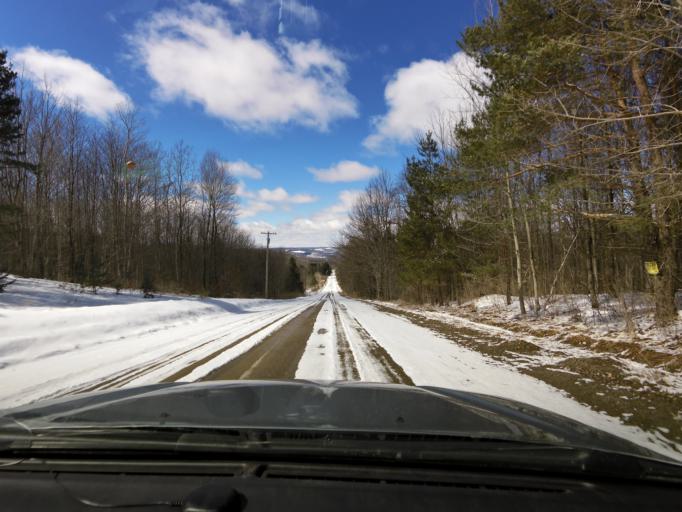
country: US
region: New York
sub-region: Cattaraugus County
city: Franklinville
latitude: 42.3429
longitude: -78.3969
